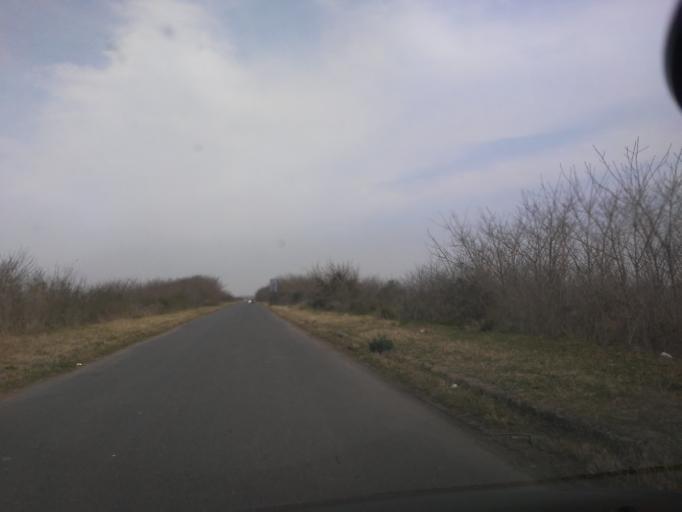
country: AR
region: Buenos Aires
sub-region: Partido de Marcos Paz
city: Marcos Paz
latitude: -34.6763
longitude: -58.8621
